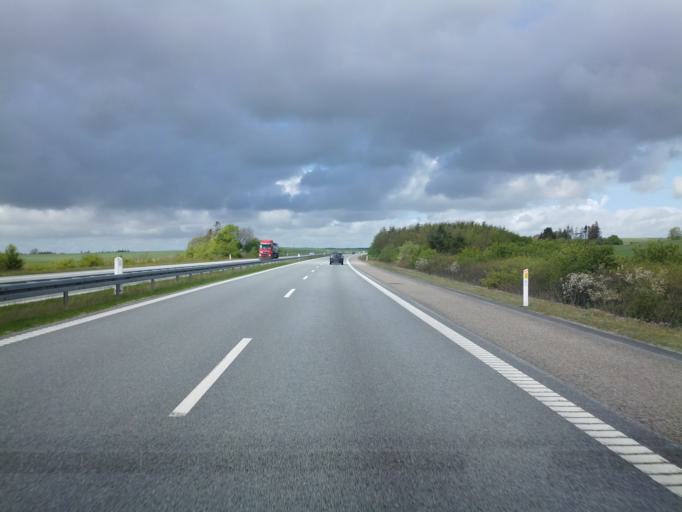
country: DK
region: North Denmark
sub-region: Bronderslev Kommune
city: Hjallerup
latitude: 57.1928
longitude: 10.1988
